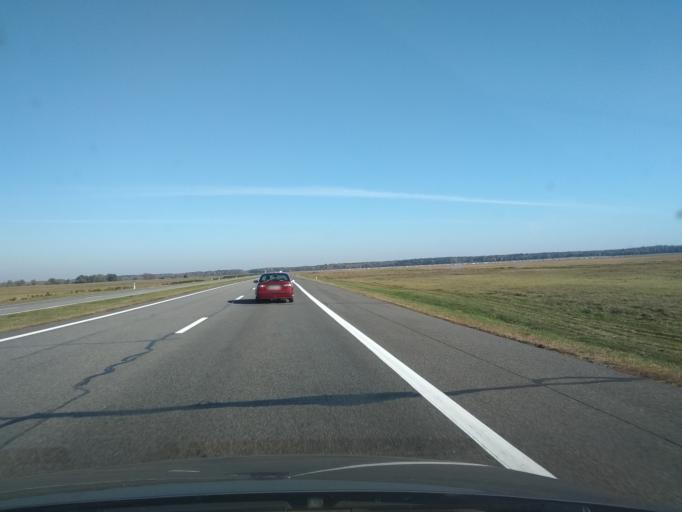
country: BY
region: Brest
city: Ivatsevichy
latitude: 52.7309
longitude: 25.4547
